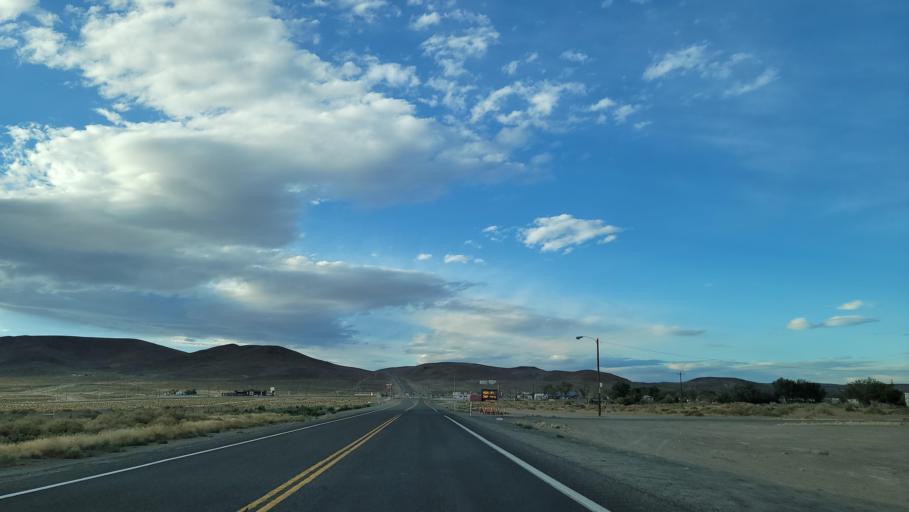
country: US
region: Nevada
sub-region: Lyon County
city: Silver Springs
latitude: 39.4088
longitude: -119.2265
